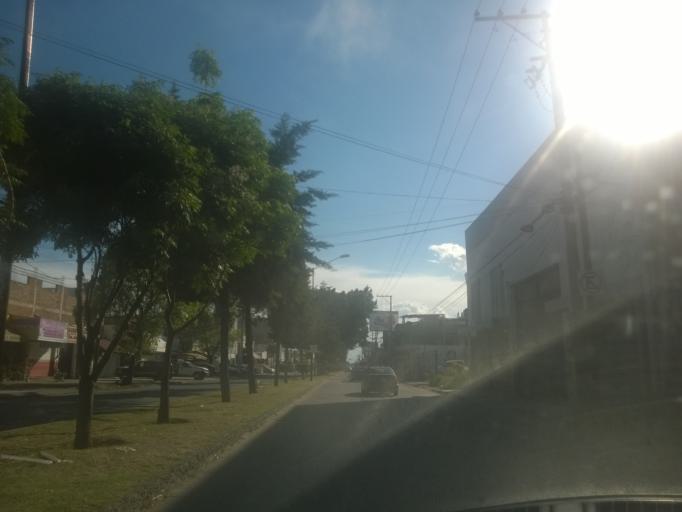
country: MX
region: Guanajuato
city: Leon
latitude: 21.1374
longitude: -101.6572
